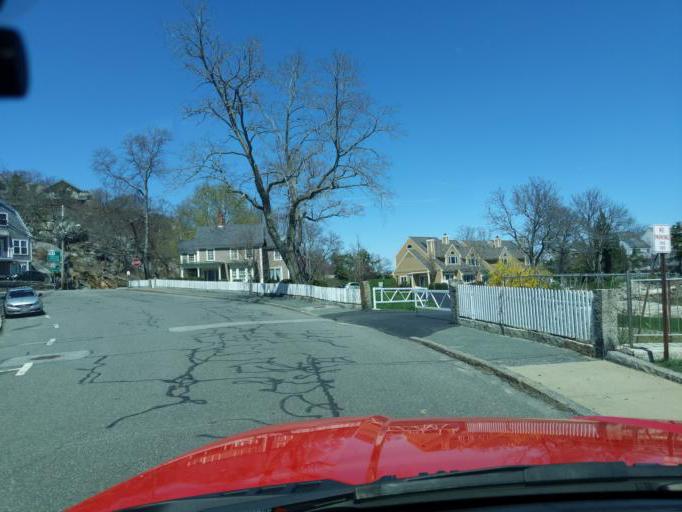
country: US
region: Massachusetts
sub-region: Essex County
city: Rockport
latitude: 42.6629
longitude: -70.6241
